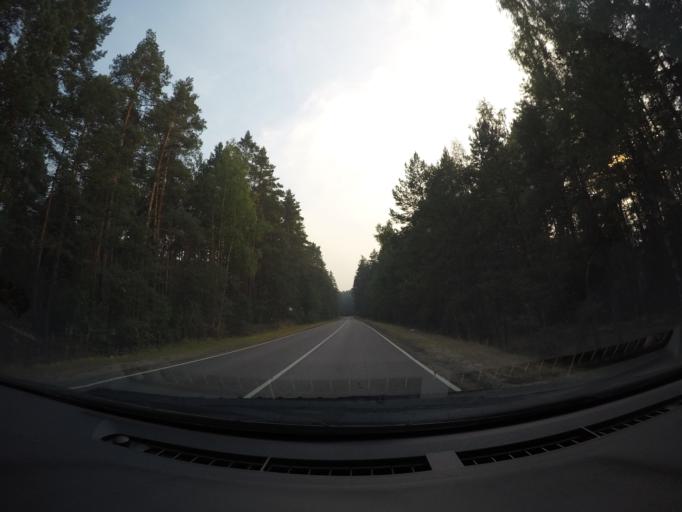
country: RU
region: Moskovskaya
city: Imeni Tsyurupy
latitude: 55.5094
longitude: 38.7178
